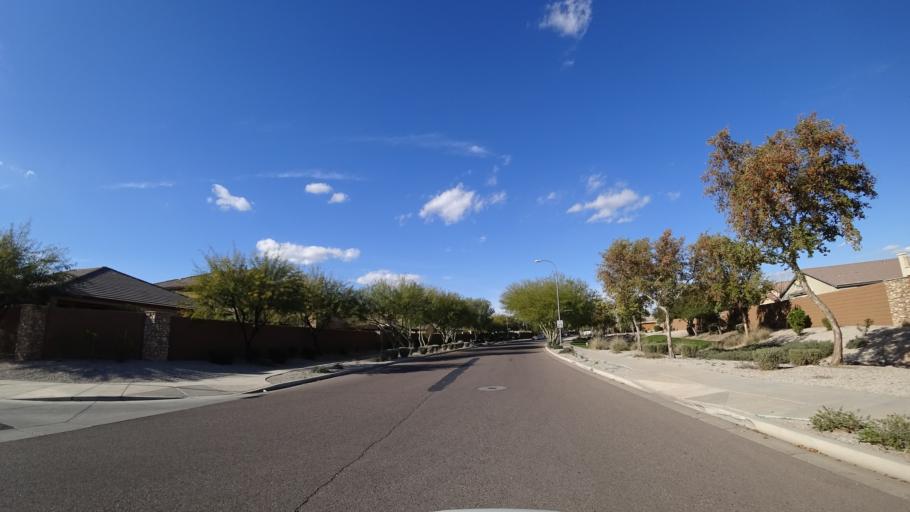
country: US
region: Arizona
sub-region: Maricopa County
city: Tolleson
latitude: 33.4154
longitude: -112.2518
